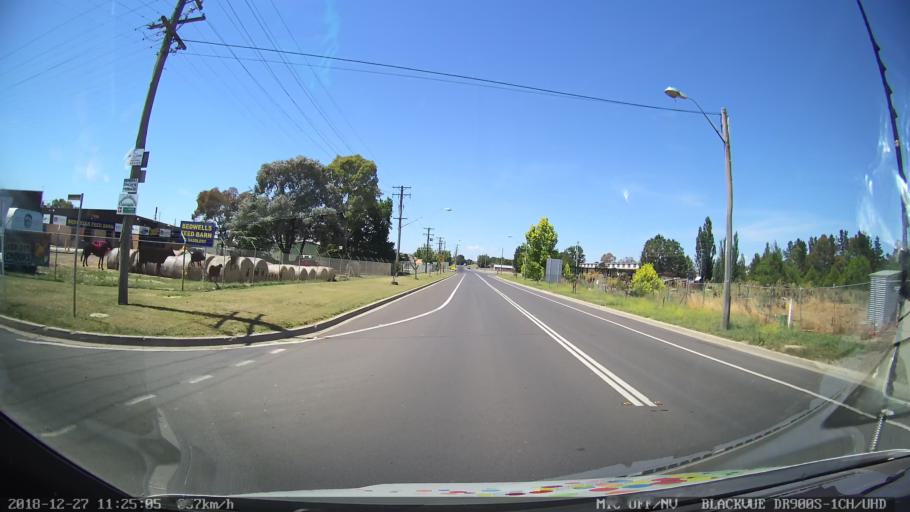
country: AU
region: New South Wales
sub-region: Bathurst Regional
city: Bathurst
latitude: -33.4387
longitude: 149.5785
